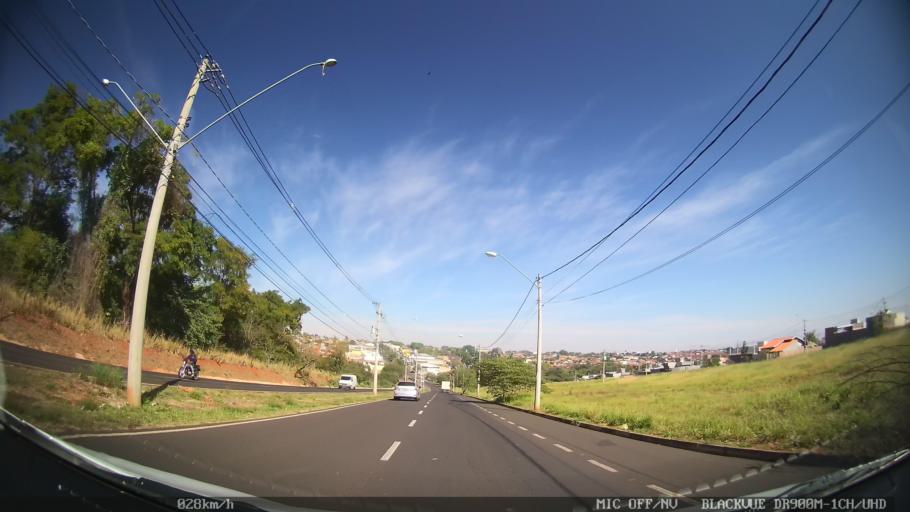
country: BR
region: Sao Paulo
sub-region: Sao Jose Do Rio Preto
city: Sao Jose do Rio Preto
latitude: -20.7683
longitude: -49.3575
